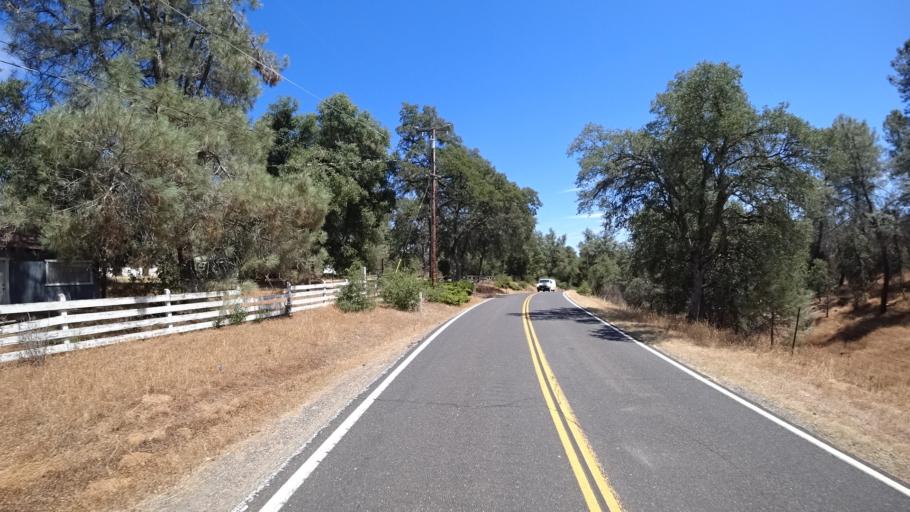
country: US
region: California
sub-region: Calaveras County
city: Mountain Ranch
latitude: 38.2439
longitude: -120.5120
